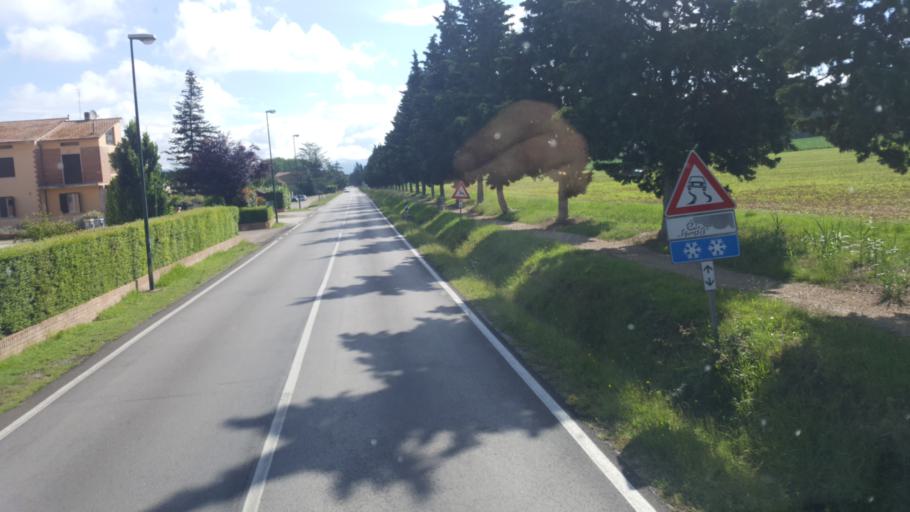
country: IT
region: Umbria
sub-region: Provincia di Perugia
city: Torgiano
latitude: 43.0205
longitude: 12.4397
